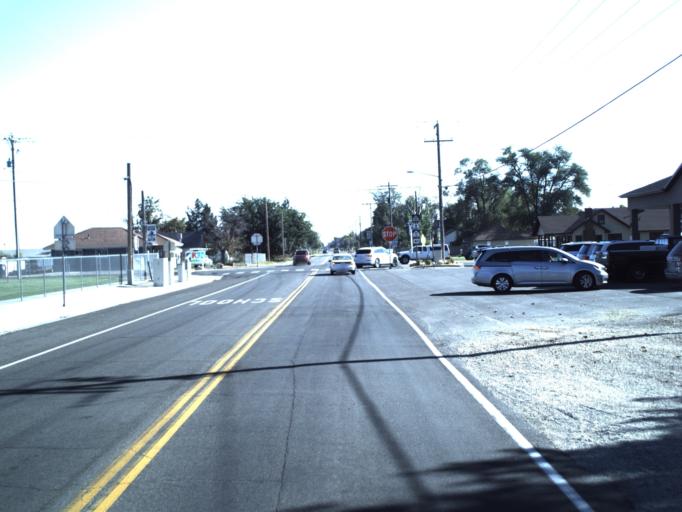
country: US
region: Utah
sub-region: Weber County
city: Hooper
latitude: 41.1647
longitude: -112.1228
